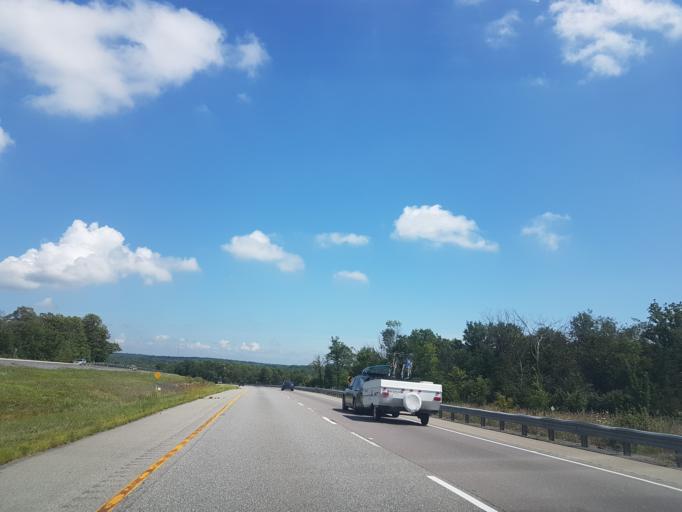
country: CA
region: Ontario
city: Kingston
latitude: 44.2873
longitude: -76.5953
